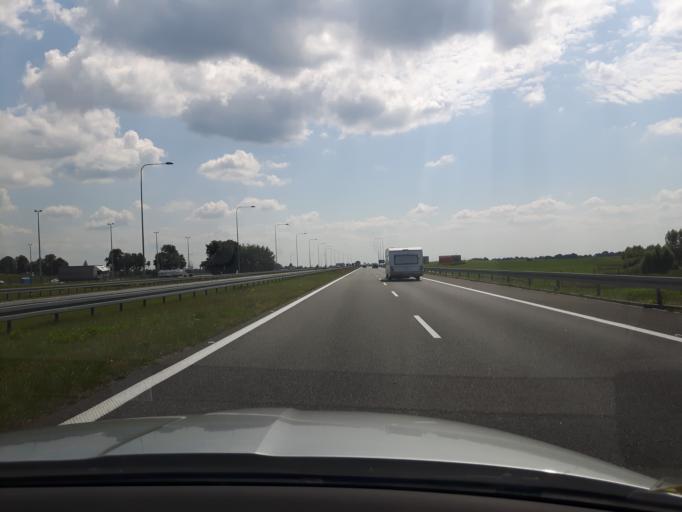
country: PL
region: Warmian-Masurian Voivodeship
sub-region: Powiat ostrodzki
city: Milomlyn
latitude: 53.8073
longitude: 19.7866
